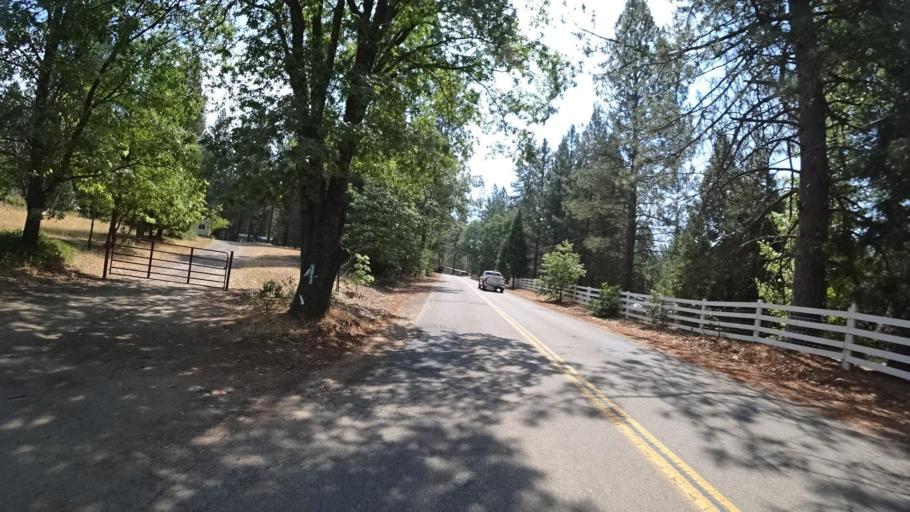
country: US
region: California
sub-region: Tuolumne County
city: Tuolumne City
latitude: 37.7368
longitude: -120.1273
